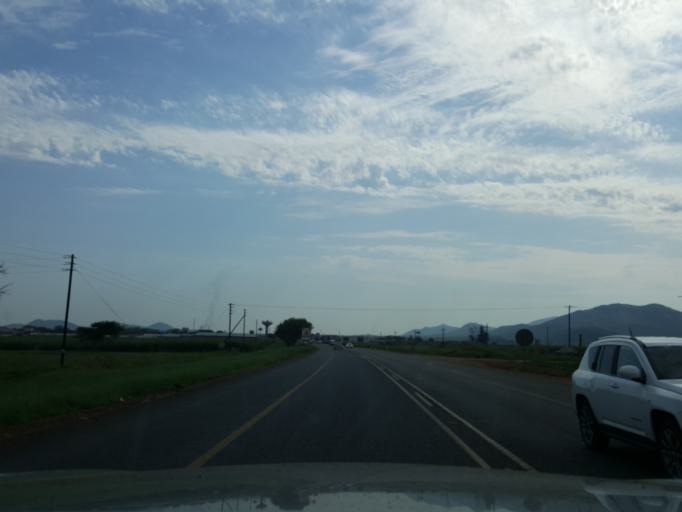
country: SZ
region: Hhohho
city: Ntfonjeni
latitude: -25.5044
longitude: 31.4981
